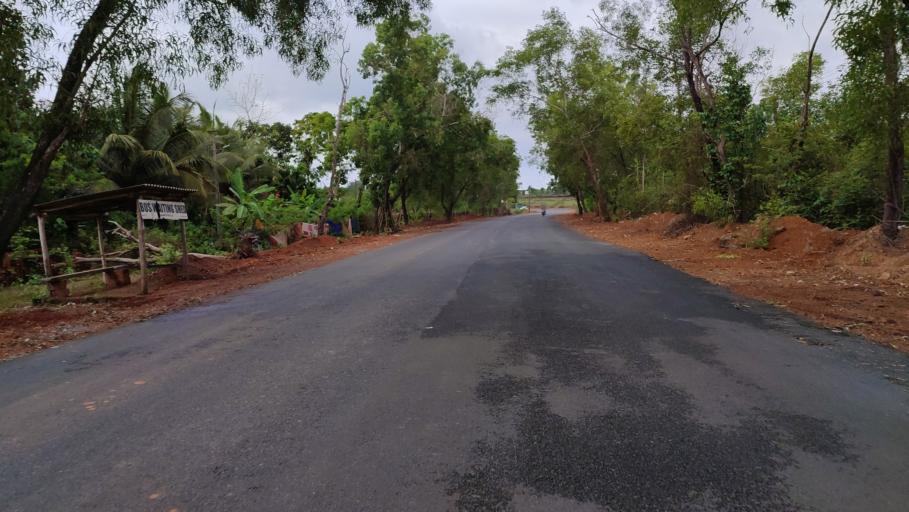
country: IN
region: Kerala
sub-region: Kasaragod District
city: Kasaragod
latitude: 12.5521
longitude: 75.0712
